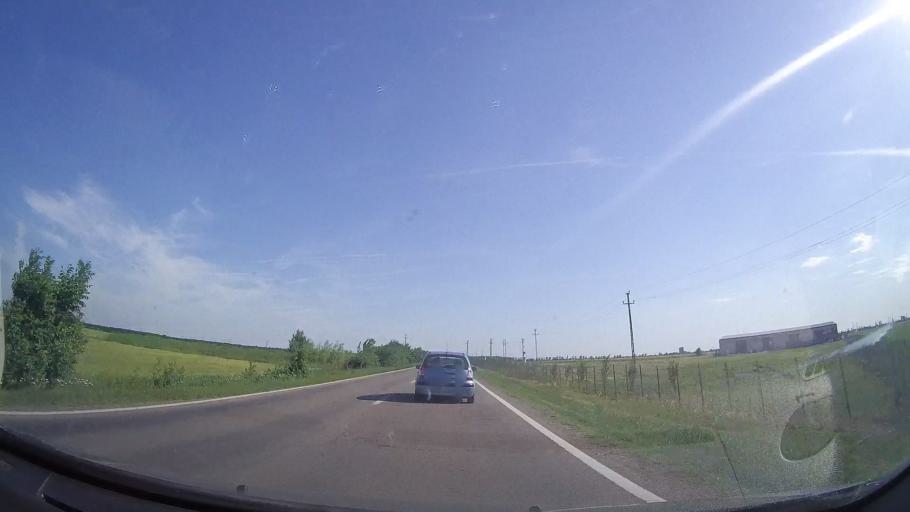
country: RO
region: Prahova
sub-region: Comuna Berceni
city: Berceni
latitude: 44.9284
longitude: 26.1033
